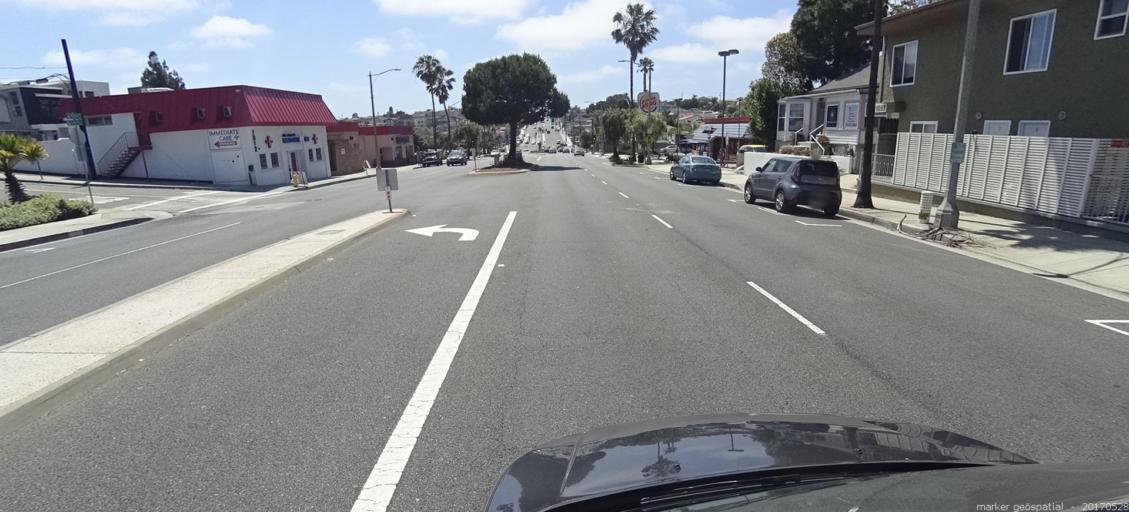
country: US
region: California
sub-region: Los Angeles County
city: Hermosa Beach
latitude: 33.8729
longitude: -118.3788
